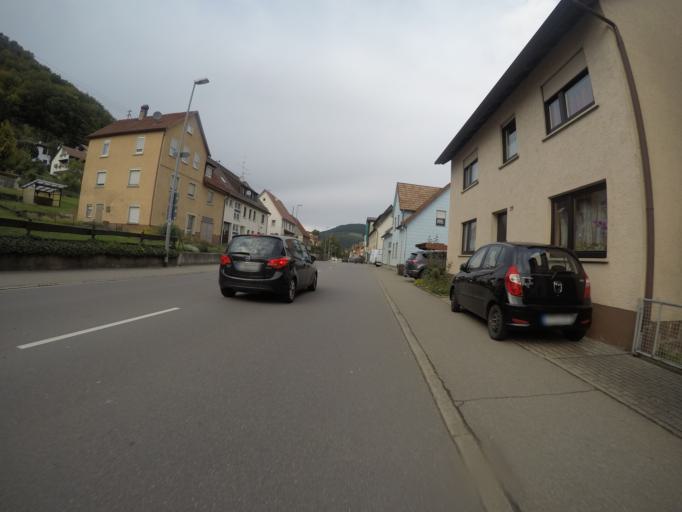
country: DE
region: Baden-Wuerttemberg
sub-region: Tuebingen Region
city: Pfullingen
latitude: 48.4281
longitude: 9.2533
